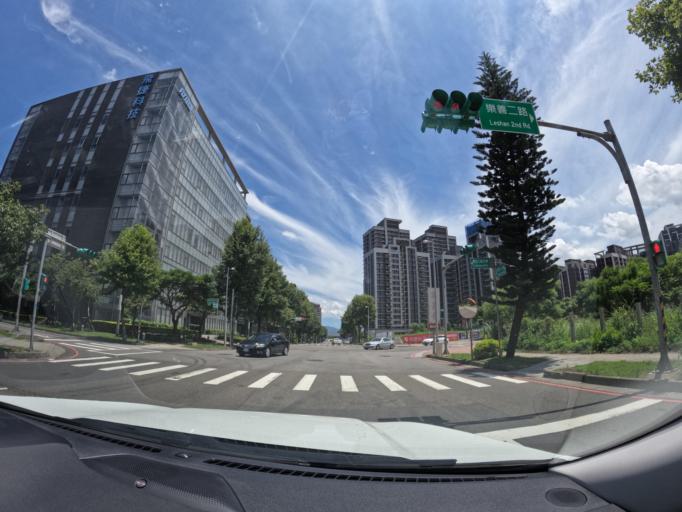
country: TW
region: Taiwan
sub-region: Taoyuan
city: Taoyuan
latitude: 25.0482
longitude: 121.3799
